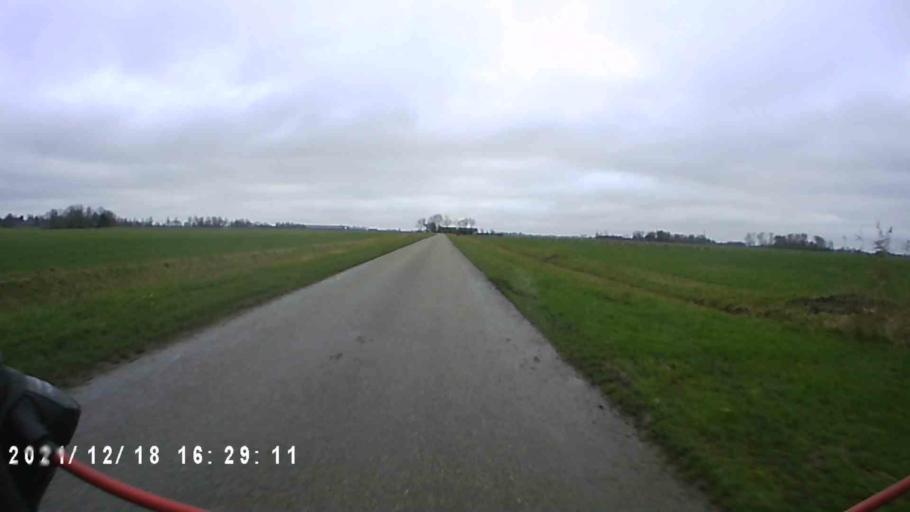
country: NL
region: Friesland
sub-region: Gemeente Dongeradeel
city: Dokkum
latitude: 53.3641
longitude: 6.0344
